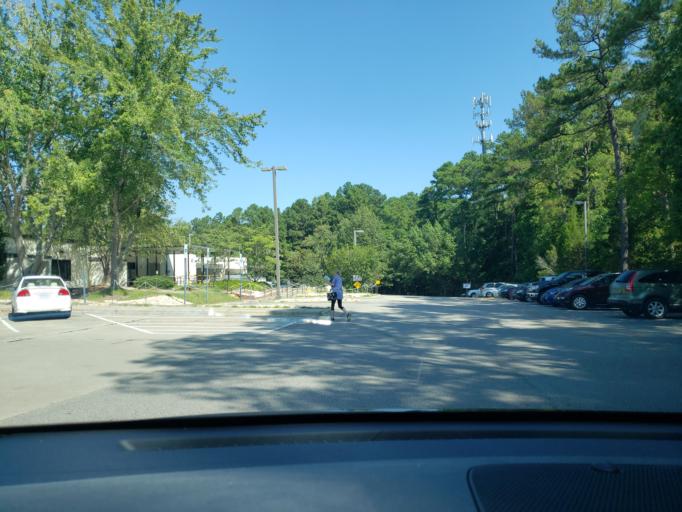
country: US
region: North Carolina
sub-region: Durham County
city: Durham
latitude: 35.9104
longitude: -78.8759
